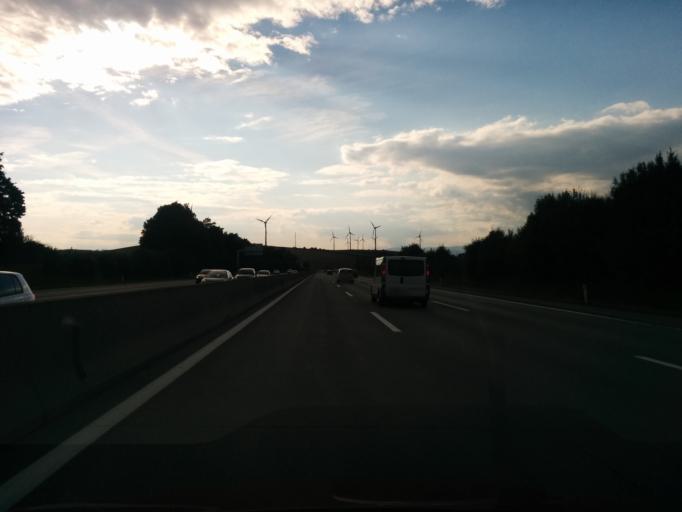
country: AT
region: Lower Austria
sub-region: Politischer Bezirk Sankt Polten
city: Sankt Margarethen an der Sierning
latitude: 48.1693
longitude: 15.4844
